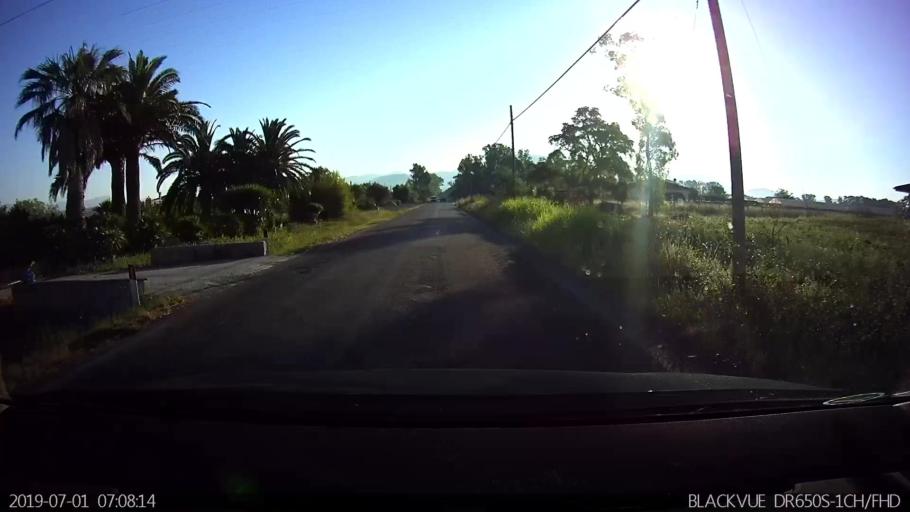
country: IT
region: Latium
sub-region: Provincia di Latina
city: Borgo Hermada
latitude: 41.2954
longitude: 13.1476
